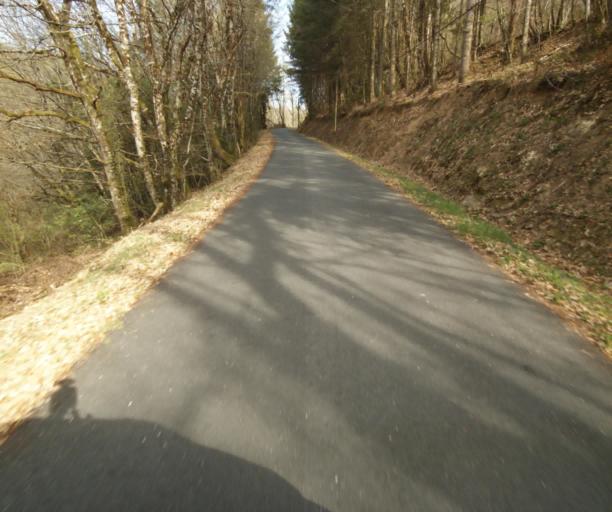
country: FR
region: Limousin
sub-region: Departement de la Correze
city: Chamboulive
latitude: 45.4284
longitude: 1.7916
